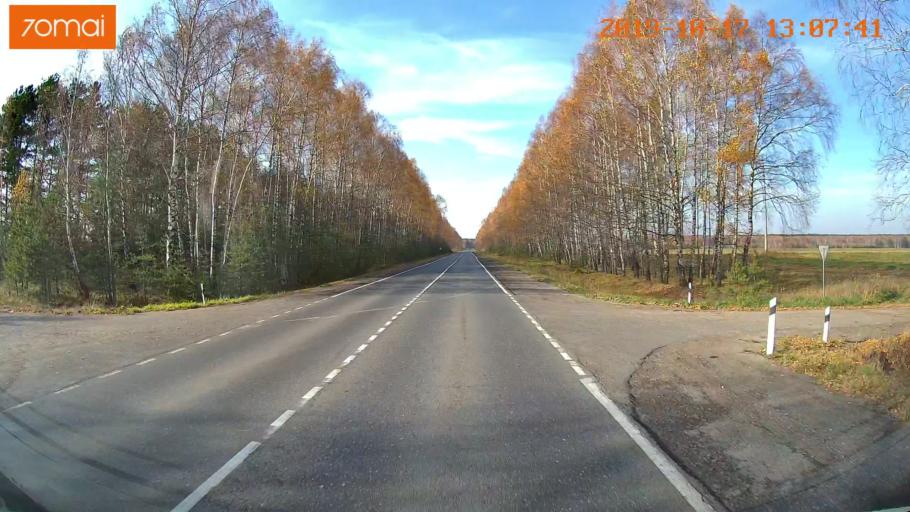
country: RU
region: Rjazan
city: Syntul
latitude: 54.9838
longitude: 41.2850
